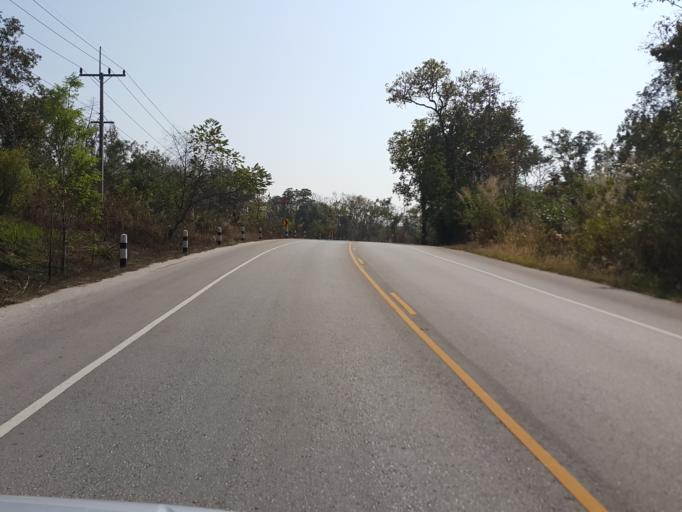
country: TH
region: Lampang
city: Mueang Pan
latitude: 18.8078
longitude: 99.5900
